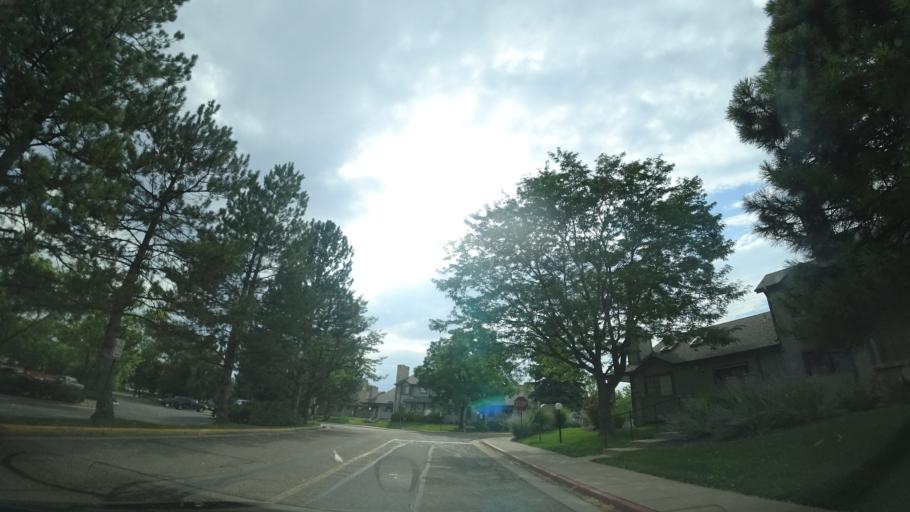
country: US
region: Colorado
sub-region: Jefferson County
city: Lakewood
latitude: 39.7133
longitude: -105.0986
